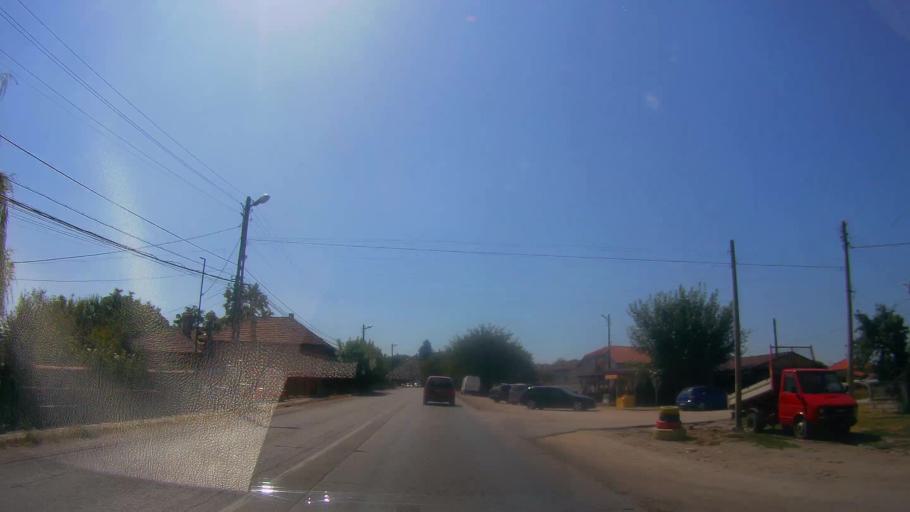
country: BG
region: Veliko Turnovo
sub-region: Obshtina Gorna Oryakhovitsa
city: Purvomaytsi
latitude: 43.1831
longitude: 25.6198
